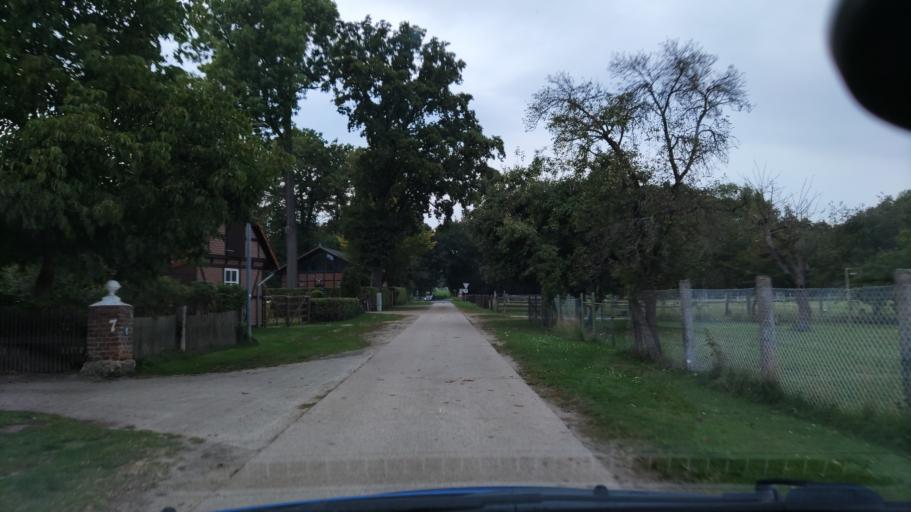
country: DE
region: Lower Saxony
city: Karwitz
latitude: 53.0879
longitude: 11.0188
